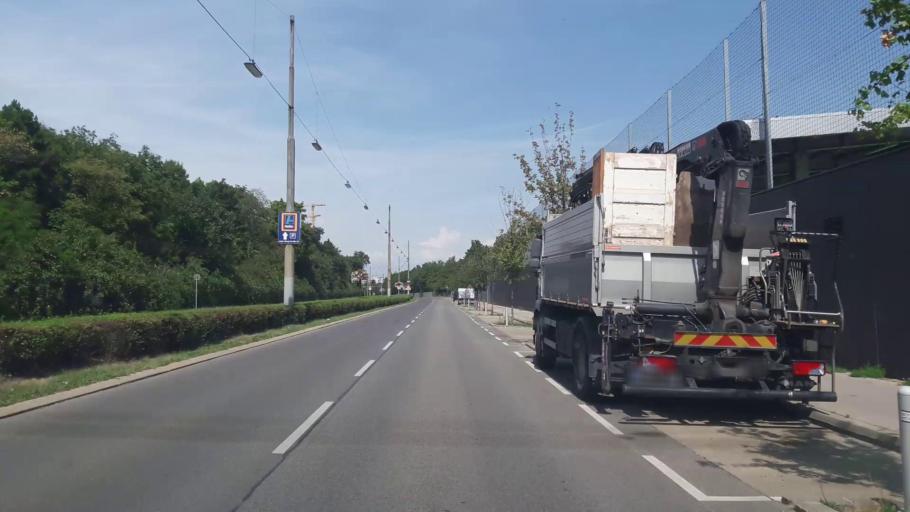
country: AT
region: Lower Austria
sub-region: Politischer Bezirk Wien-Umgebung
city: Leopoldsdorf
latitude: 48.1590
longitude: 16.3944
